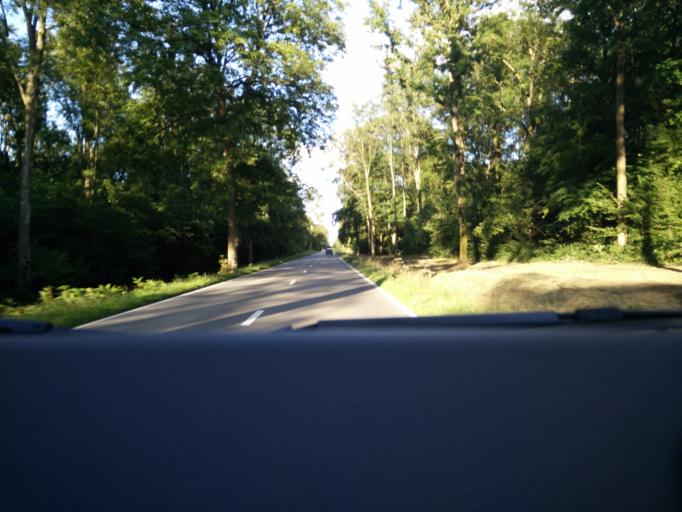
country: BE
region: Wallonia
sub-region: Province de Namur
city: Florennes
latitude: 50.2163
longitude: 4.6229
